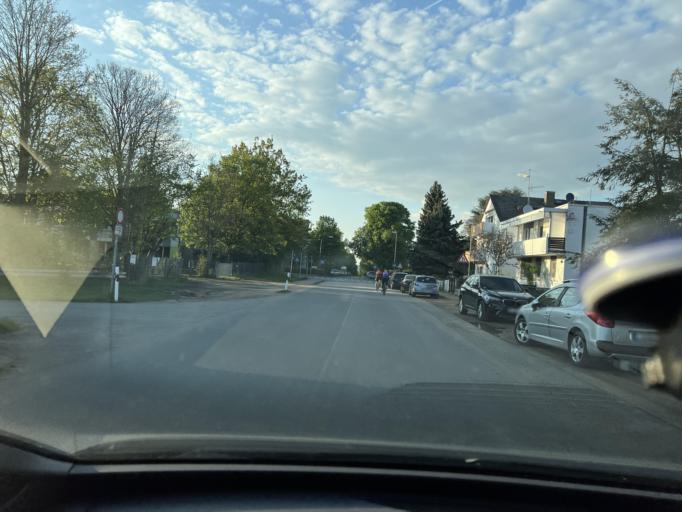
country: DE
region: Hesse
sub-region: Regierungsbezirk Darmstadt
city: Offenbach
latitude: 50.0918
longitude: 8.7880
